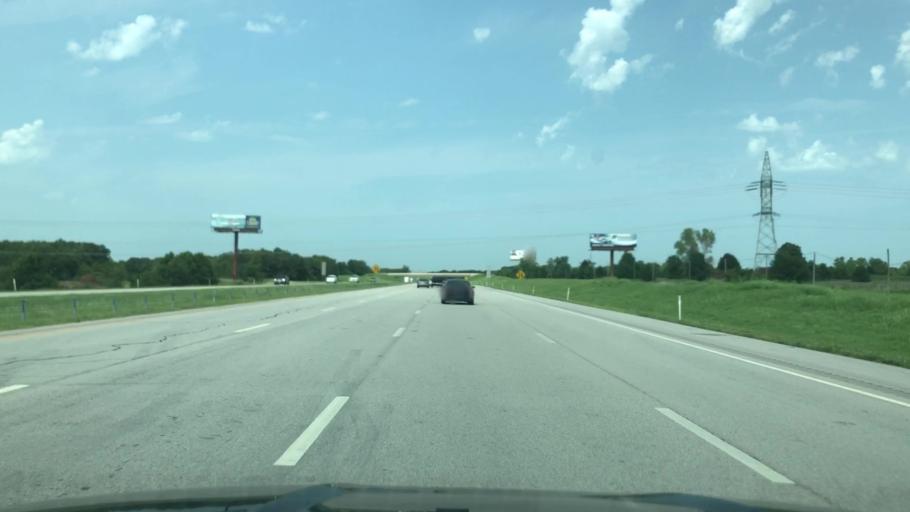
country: US
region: Oklahoma
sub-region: Rogers County
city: Catoosa
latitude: 36.1707
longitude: -95.7319
